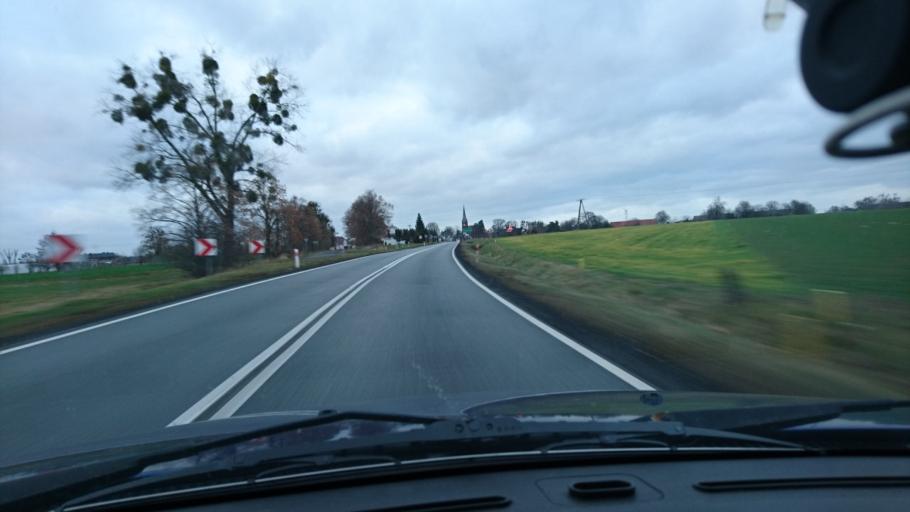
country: PL
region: Opole Voivodeship
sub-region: Powiat kluczborski
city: Kluczbork
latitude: 51.0233
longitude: 18.1939
